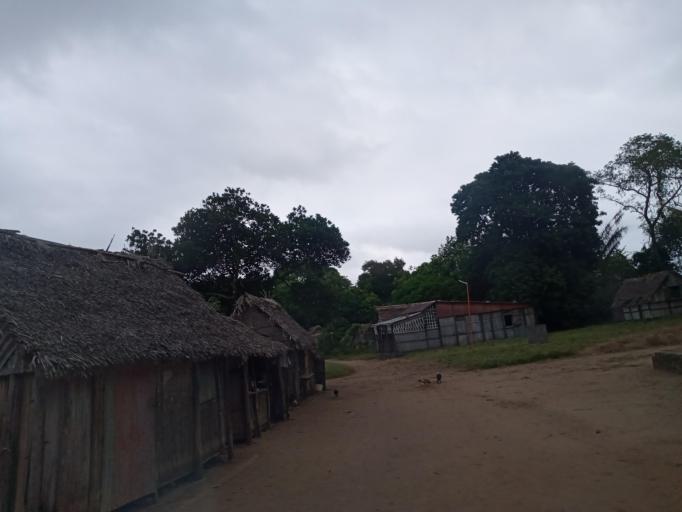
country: MG
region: Atsimo-Atsinanana
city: Vohipaho
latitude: -24.0434
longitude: 47.4394
